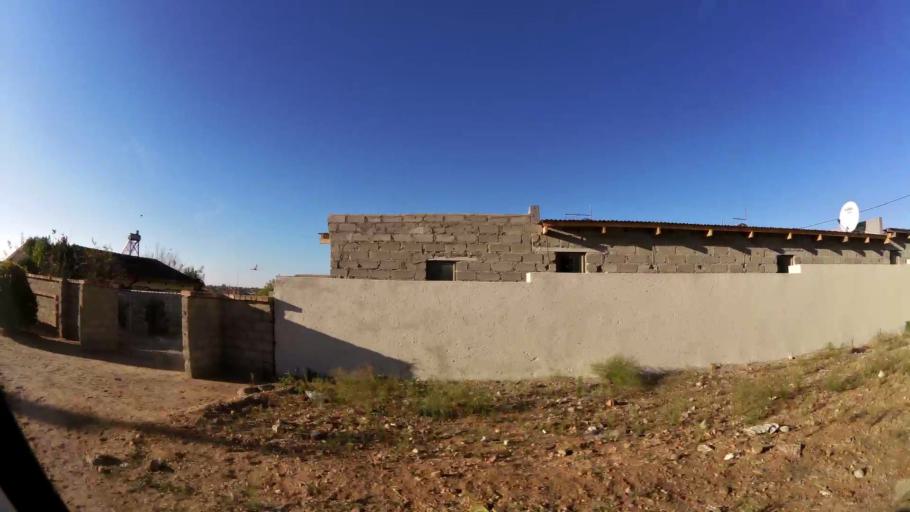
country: ZA
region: Limpopo
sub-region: Capricorn District Municipality
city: Polokwane
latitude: -23.8481
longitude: 29.3559
